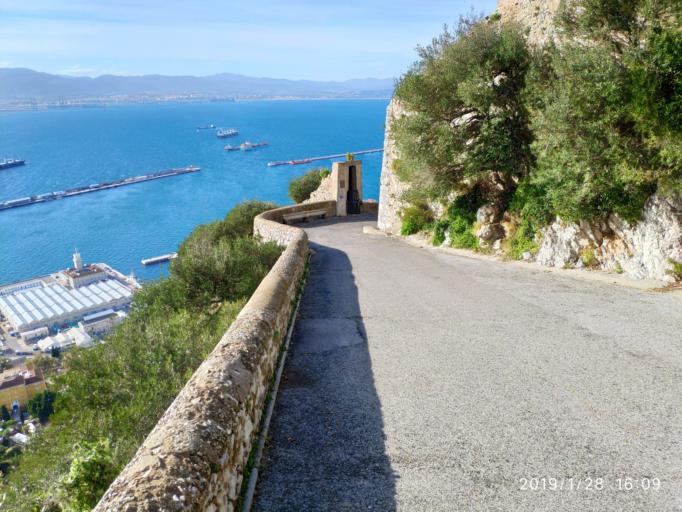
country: GI
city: Gibraltar
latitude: 36.1320
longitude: -5.3483
